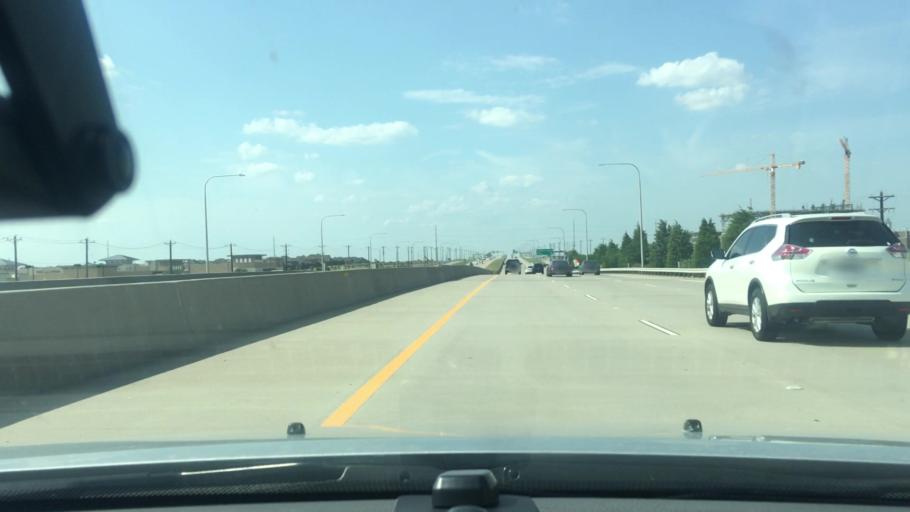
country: US
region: Texas
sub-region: Collin County
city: Frisco
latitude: 33.1749
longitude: -96.8396
